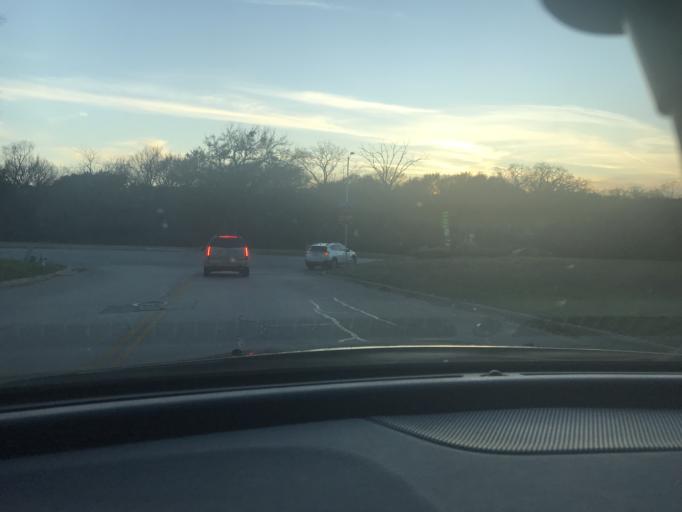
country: US
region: Texas
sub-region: Tarrant County
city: Arlington
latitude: 32.7656
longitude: -97.1038
